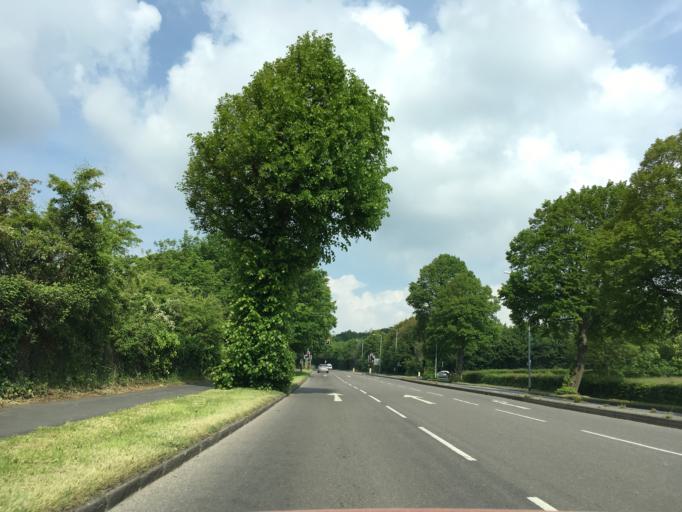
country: GB
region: England
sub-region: North Somerset
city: Easton-in-Gordano
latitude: 51.4858
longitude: -2.6543
